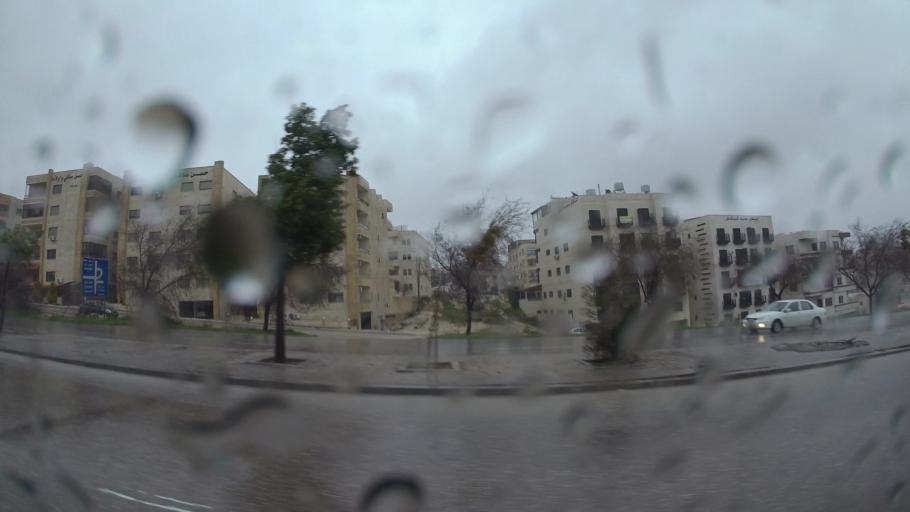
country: JO
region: Amman
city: Al Jubayhah
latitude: 32.0233
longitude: 35.8927
